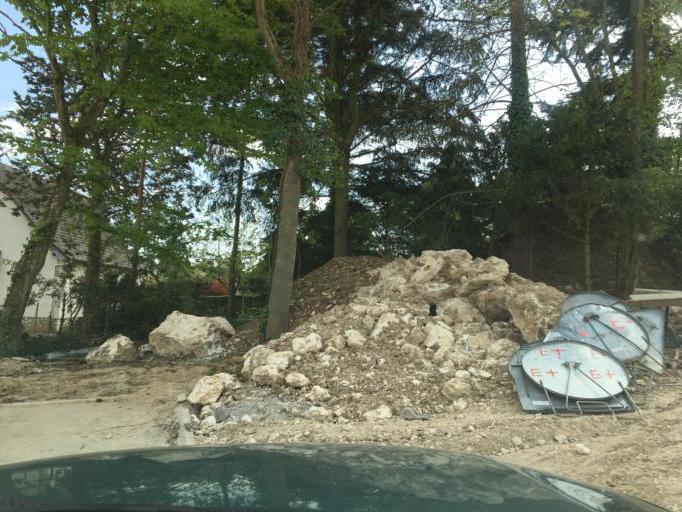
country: FR
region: Centre
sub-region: Departement du Loiret
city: Beaugency
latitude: 47.7834
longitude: 1.6241
